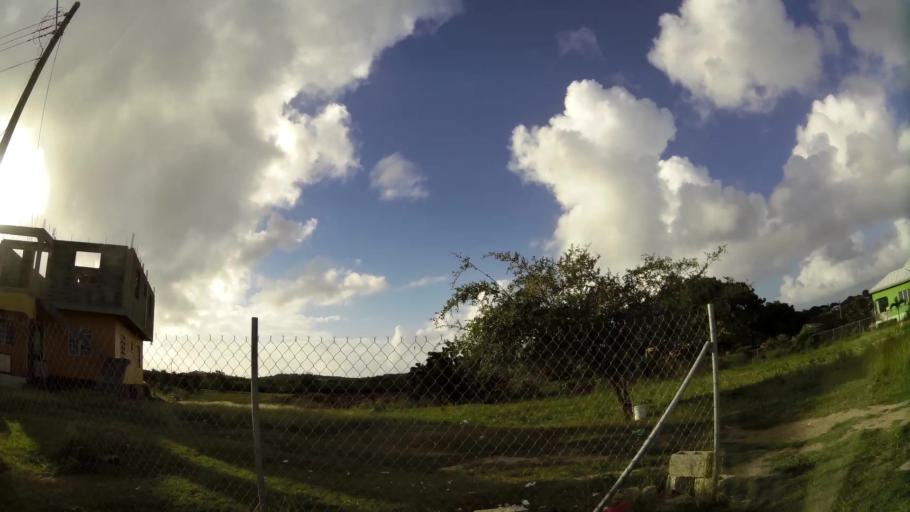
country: AG
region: Saint John
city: Saint John's
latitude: 17.1559
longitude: -61.8246
